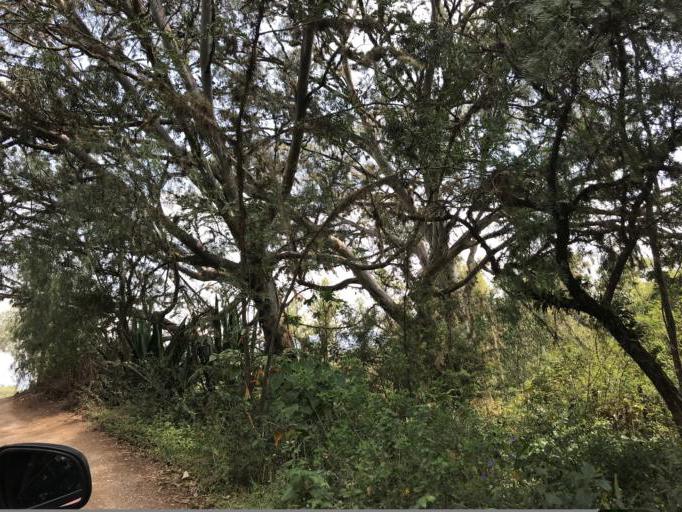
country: CO
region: Boyaca
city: Villa de Leiva
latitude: 5.6511
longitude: -73.5759
